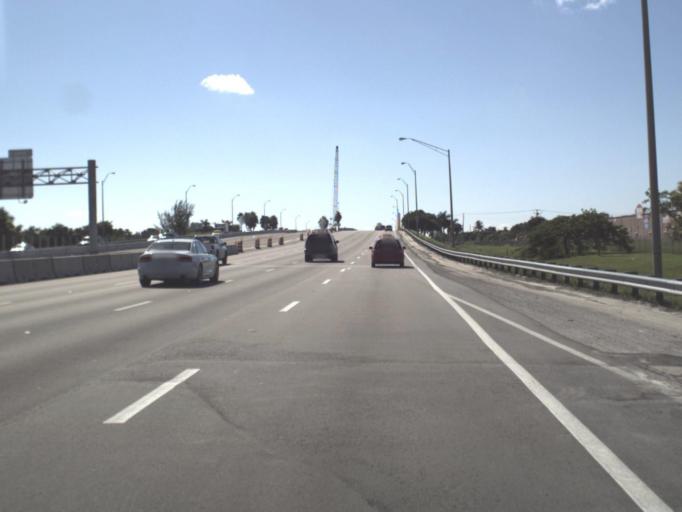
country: US
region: Florida
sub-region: Miami-Dade County
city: Palmetto Estates
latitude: 25.6165
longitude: -80.3788
